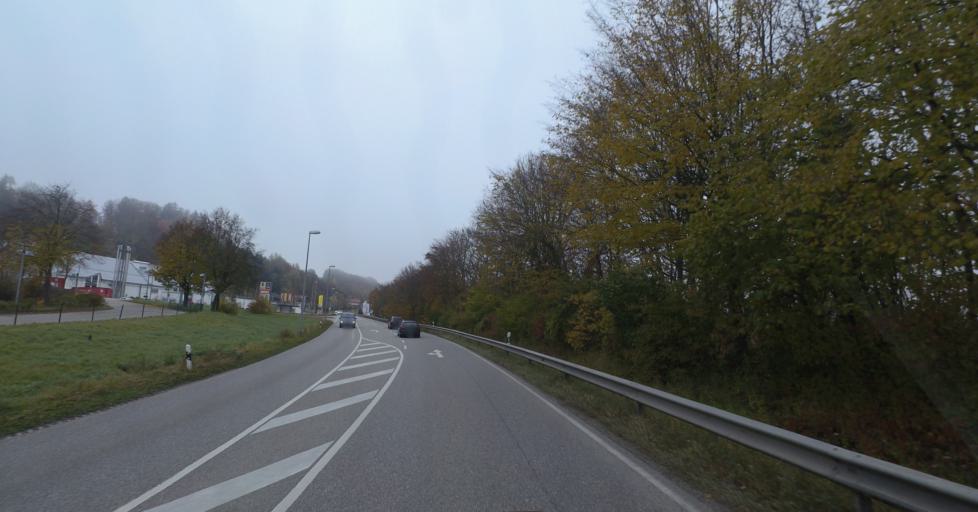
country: DE
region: Bavaria
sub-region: Upper Bavaria
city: Trostberg an der Alz
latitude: 48.0195
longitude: 12.5363
